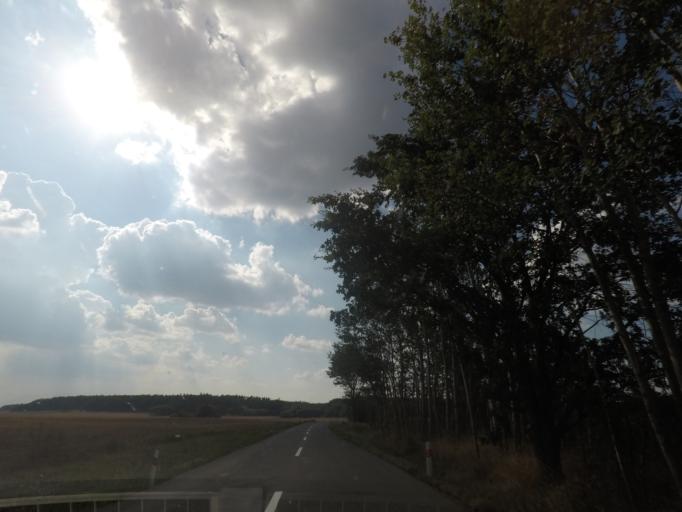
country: CZ
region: Kralovehradecky
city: Trebechovice pod Orebem
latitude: 50.2178
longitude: 15.9839
